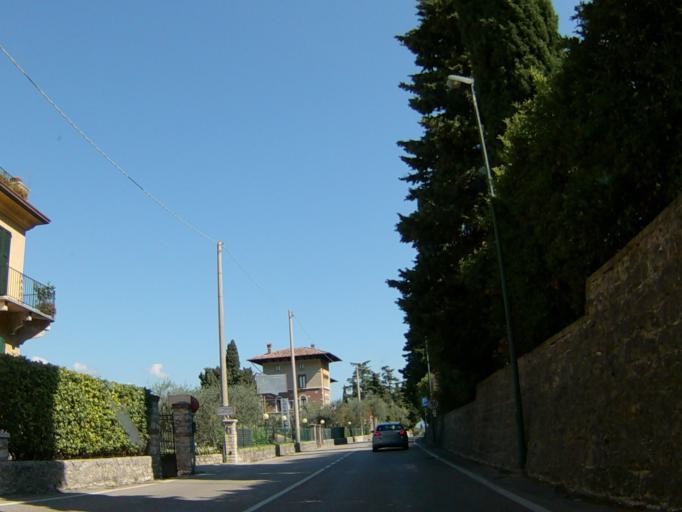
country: IT
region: Veneto
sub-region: Provincia di Verona
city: Brenzone
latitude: 45.6903
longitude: 10.7523
